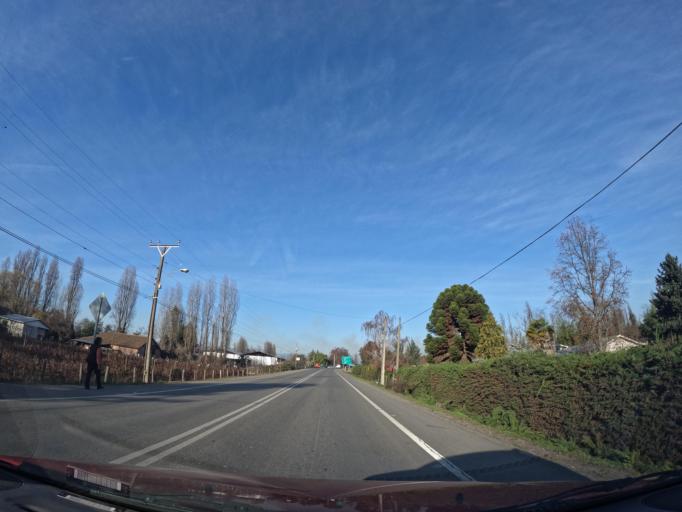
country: CL
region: Maule
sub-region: Provincia de Talca
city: San Clemente
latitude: -35.6237
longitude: -71.4837
